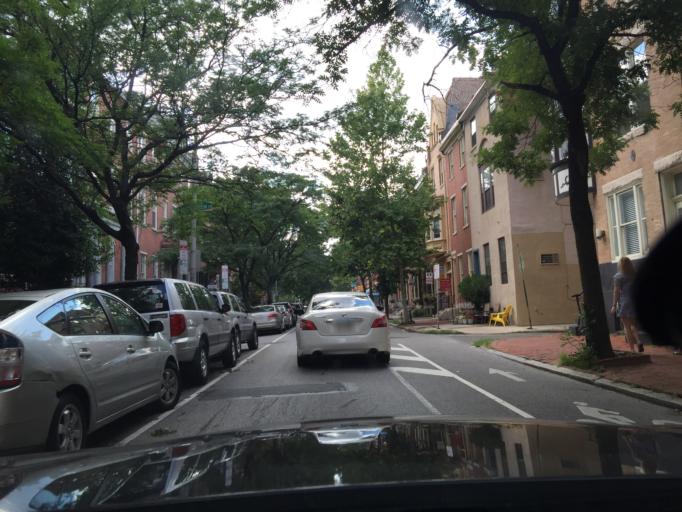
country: US
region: Pennsylvania
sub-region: Philadelphia County
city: Philadelphia
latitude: 39.9460
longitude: -75.1569
